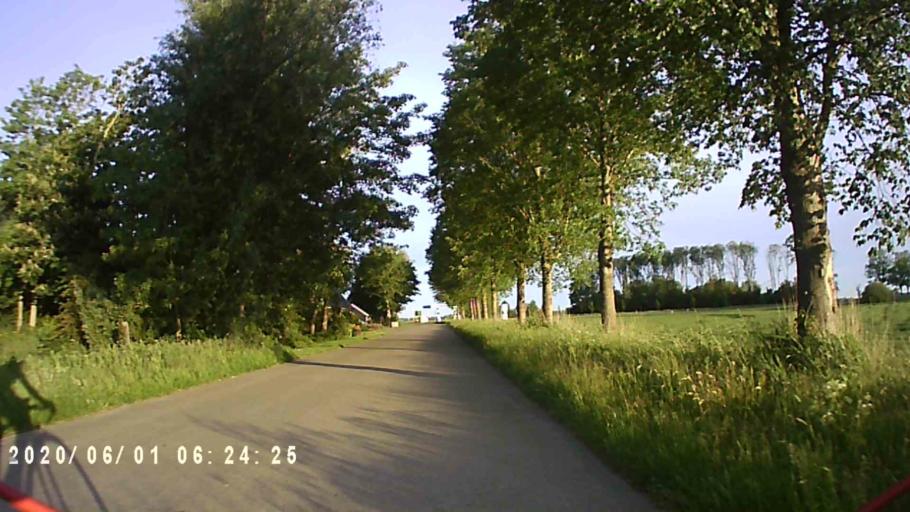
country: NL
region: Friesland
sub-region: Gemeente Kollumerland en Nieuwkruisland
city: Kollum
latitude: 53.2668
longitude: 6.2098
